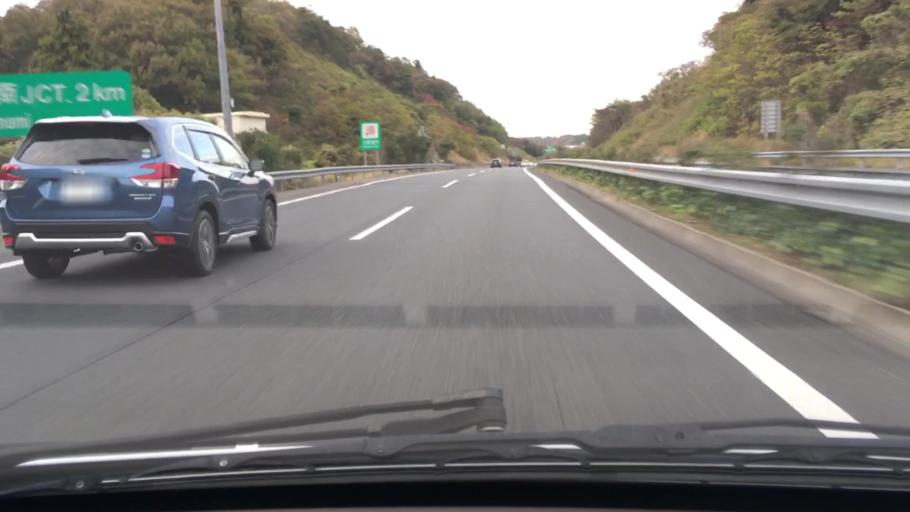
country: JP
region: Chiba
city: Kisarazu
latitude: 35.3341
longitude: 139.9451
